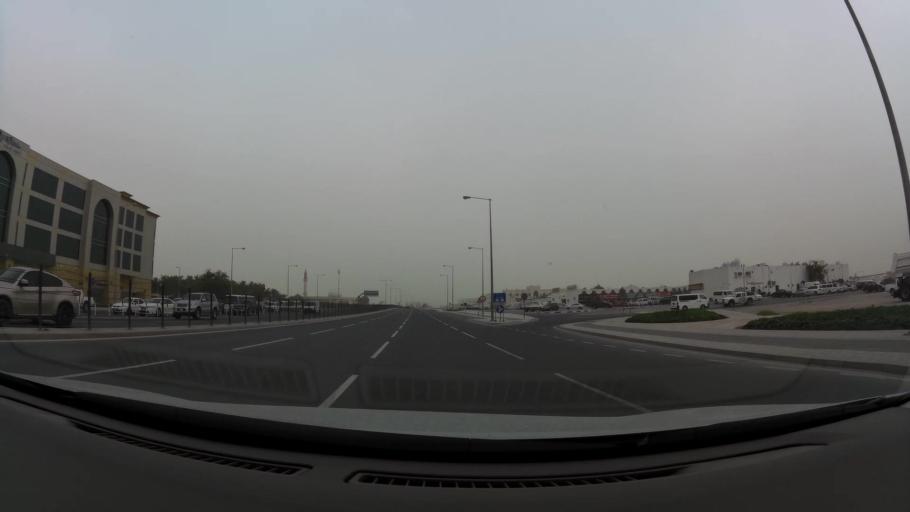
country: QA
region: Baladiyat ad Dawhah
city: Doha
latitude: 25.2485
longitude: 51.4722
